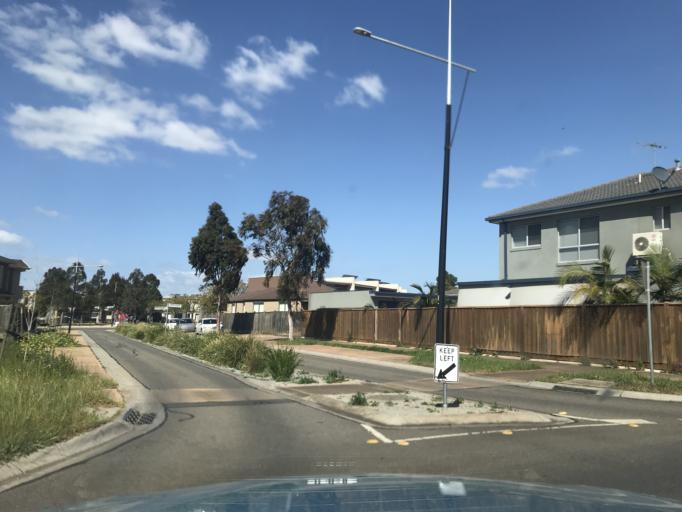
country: AU
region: Victoria
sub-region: Wyndham
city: Williams Landing
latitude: -37.8540
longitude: 144.7348
